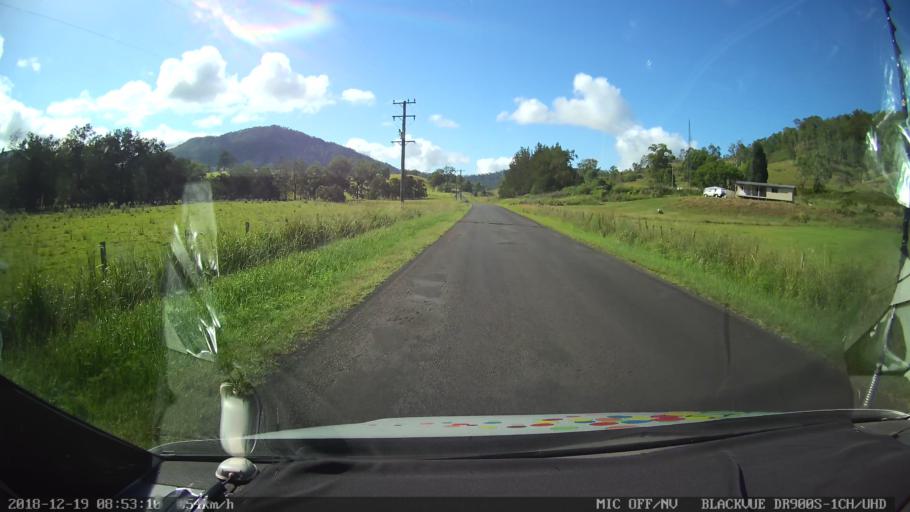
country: AU
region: New South Wales
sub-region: Kyogle
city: Kyogle
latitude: -28.3987
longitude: 152.9769
